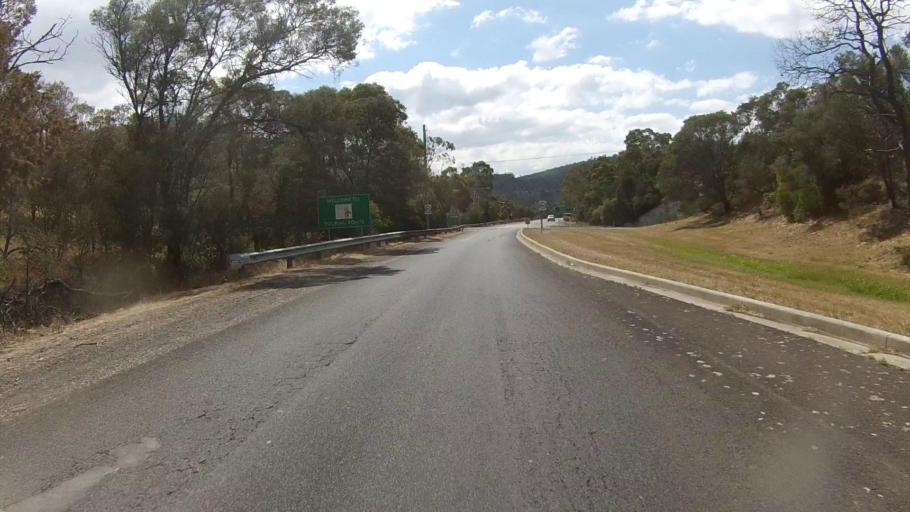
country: AU
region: Tasmania
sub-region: Clarence
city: Cambridge
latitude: -42.8457
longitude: 147.4196
